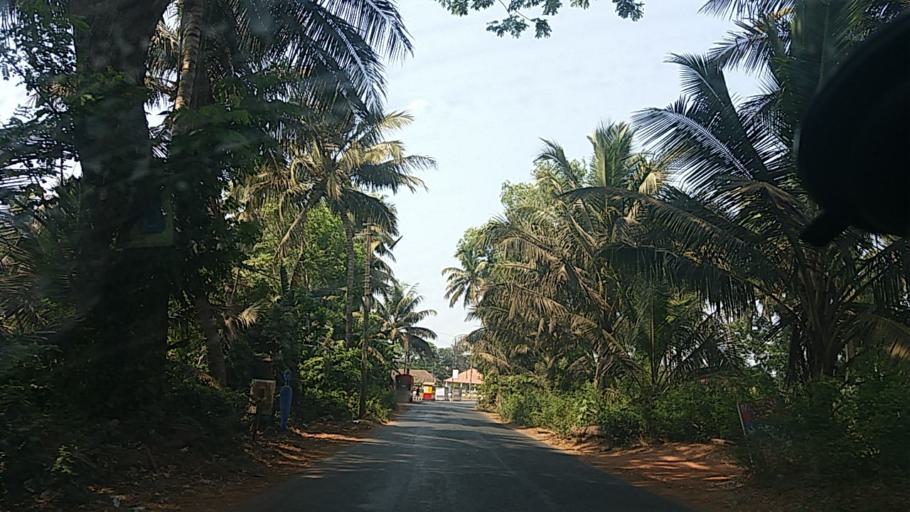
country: IN
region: Goa
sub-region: North Goa
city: Saligao
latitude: 15.5445
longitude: 73.7892
